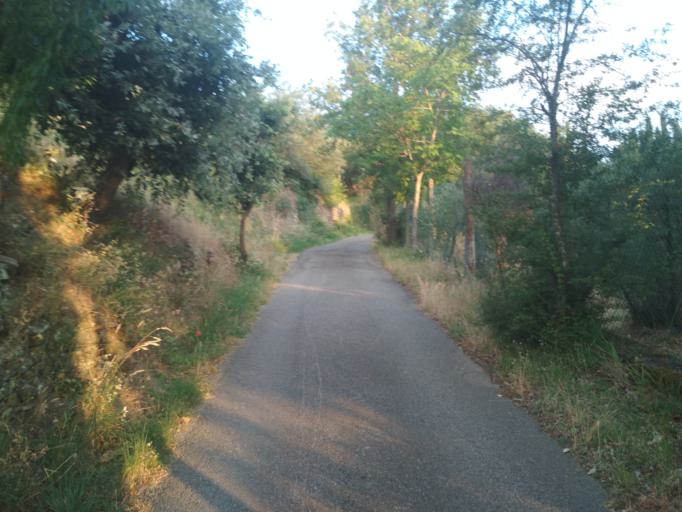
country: IT
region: Tuscany
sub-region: Province of Arezzo
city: Castiglion Fiorentino
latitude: 43.3139
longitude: 11.9296
